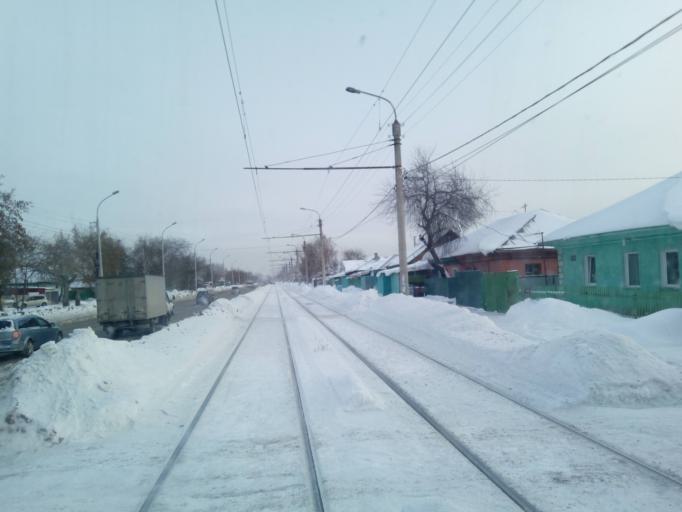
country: RU
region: Novosibirsk
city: Tolmachevo
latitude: 54.9804
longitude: 82.8375
